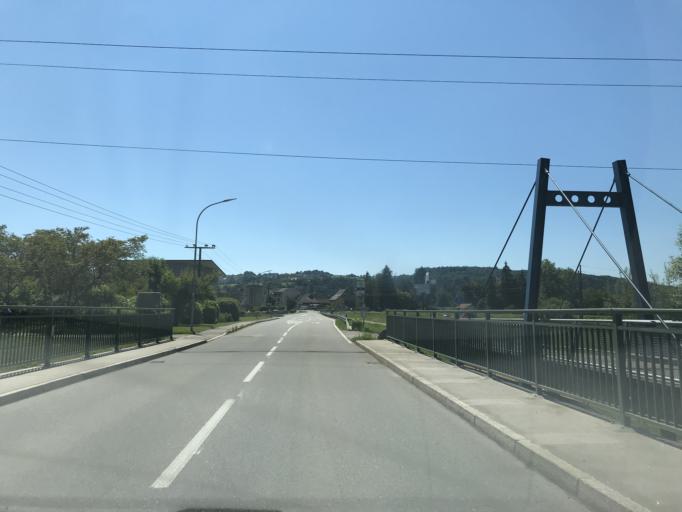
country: DE
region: Baden-Wuerttemberg
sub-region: Freiburg Region
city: Maulburg
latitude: 47.6513
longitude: 7.8000
